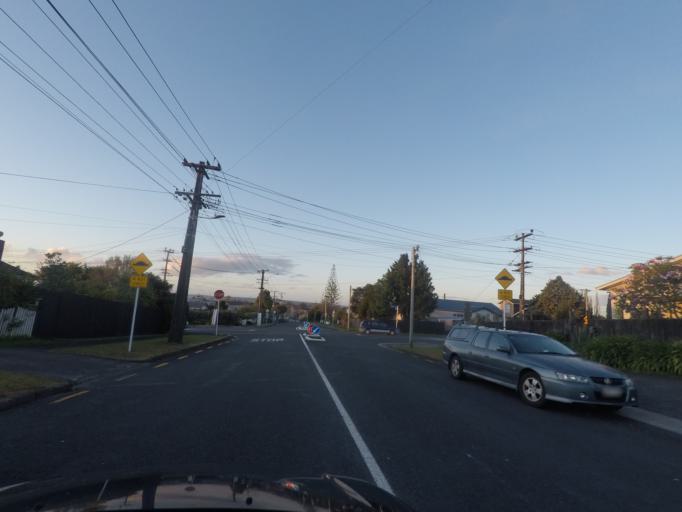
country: NZ
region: Auckland
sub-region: Auckland
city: Waitakere
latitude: -36.9043
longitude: 174.6697
